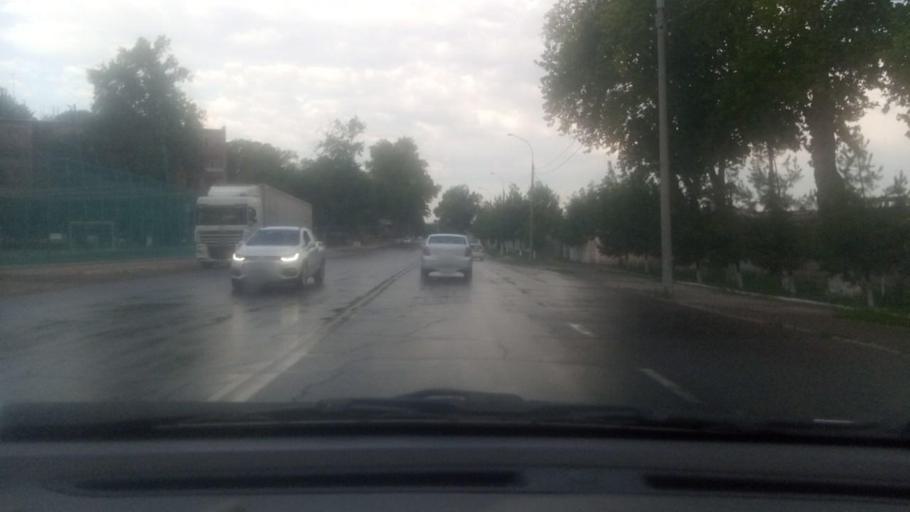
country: UZ
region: Toshkent Shahri
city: Tashkent
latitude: 41.2986
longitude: 69.1865
